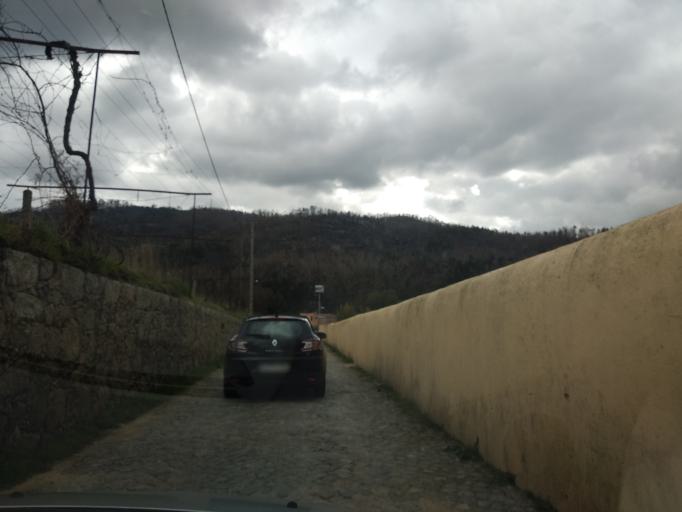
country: PT
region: Braga
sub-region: Braga
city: Braga
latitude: 41.5255
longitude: -8.4127
